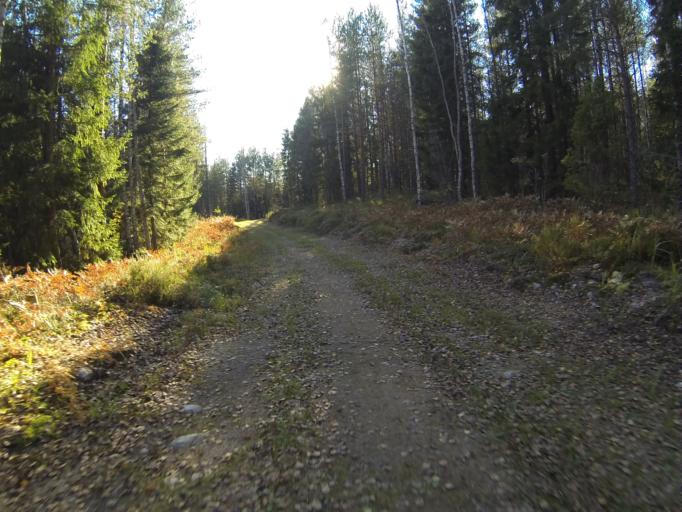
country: FI
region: Varsinais-Suomi
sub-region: Salo
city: Saerkisalo
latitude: 60.2222
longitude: 22.9427
